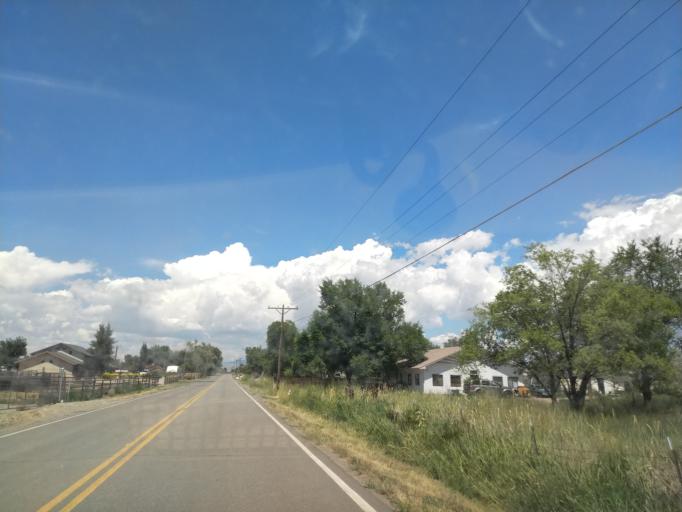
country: US
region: Colorado
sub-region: Mesa County
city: Redlands
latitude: 39.1219
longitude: -108.6639
